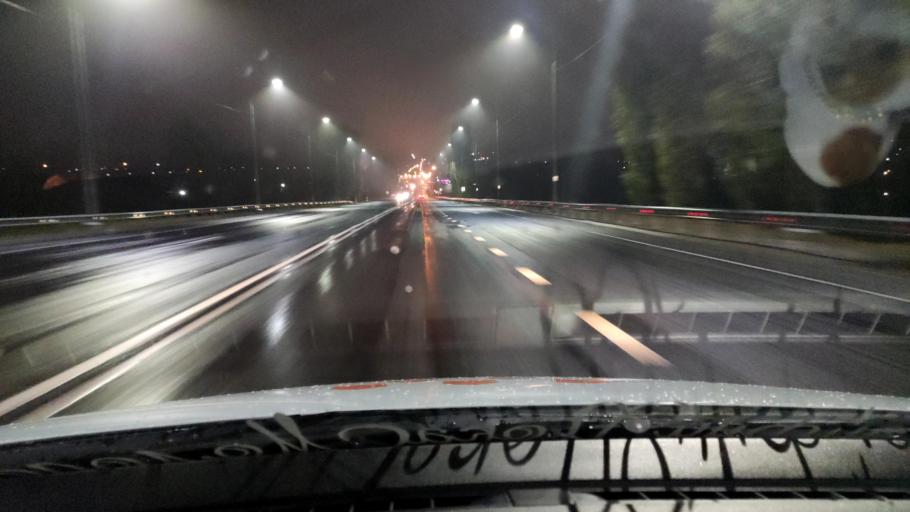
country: RU
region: Voronezj
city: Devitsa
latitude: 51.6336
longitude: 38.9578
